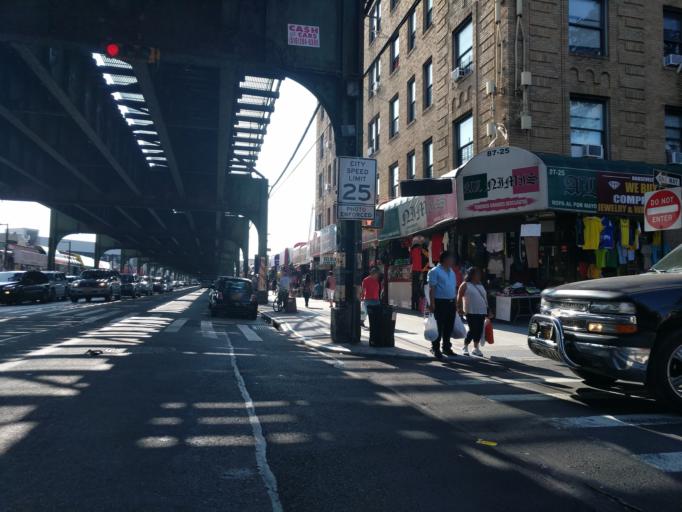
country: US
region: New York
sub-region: Queens County
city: Long Island City
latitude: 40.7483
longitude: -73.8780
